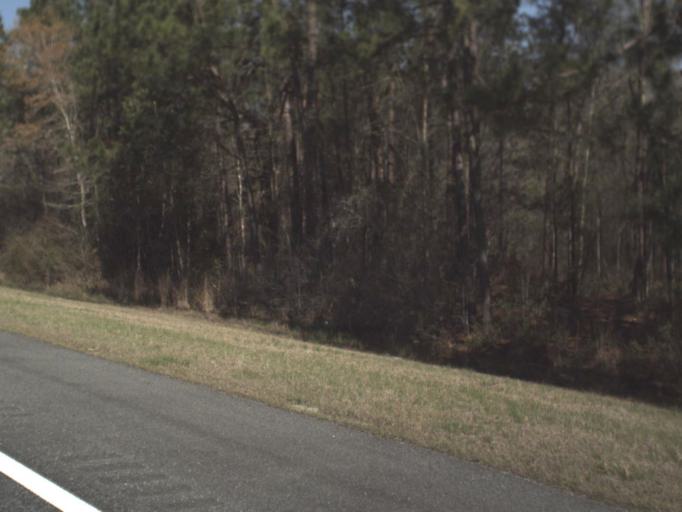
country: US
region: Florida
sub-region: Jackson County
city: Marianna
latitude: 30.7001
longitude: -85.1344
